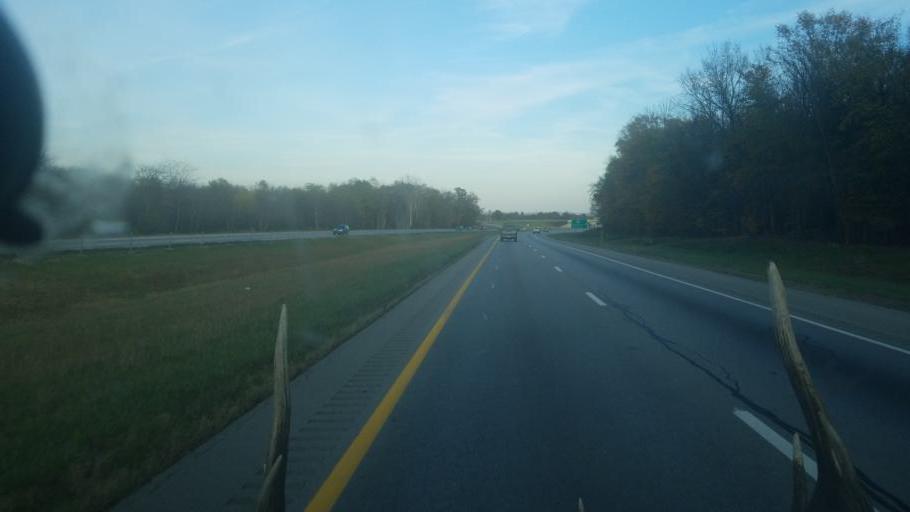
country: US
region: Ohio
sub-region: Licking County
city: Etna
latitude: 39.9455
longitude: -82.6086
